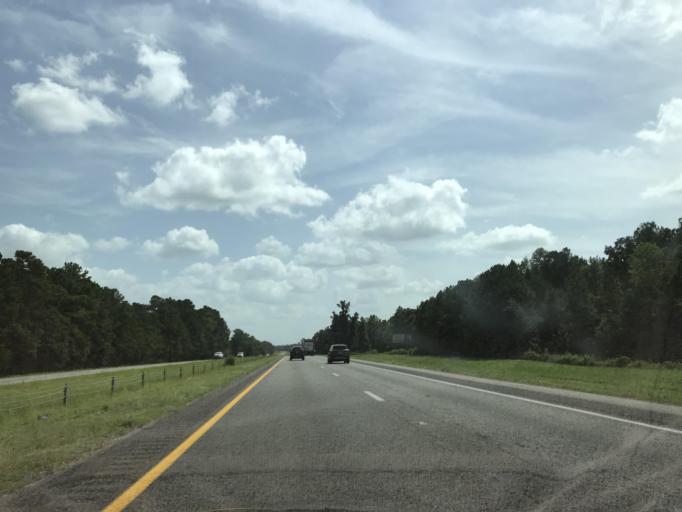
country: US
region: North Carolina
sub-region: Pender County
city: Burgaw
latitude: 34.6493
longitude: -77.9407
